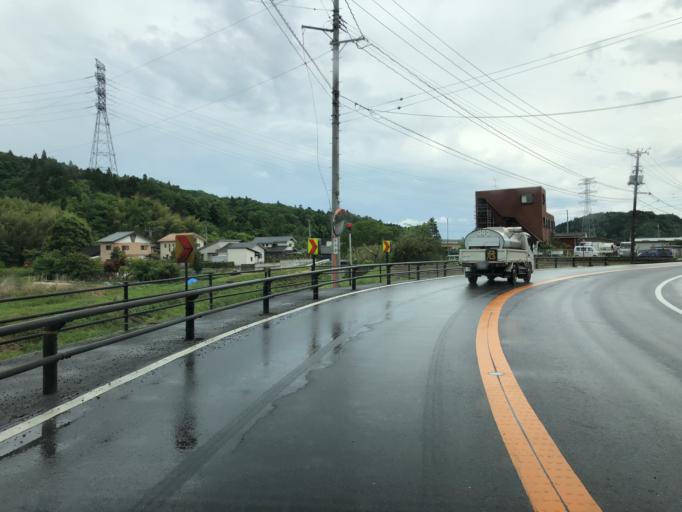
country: JP
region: Ibaraki
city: Kitaibaraki
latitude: 36.9413
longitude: 140.7694
